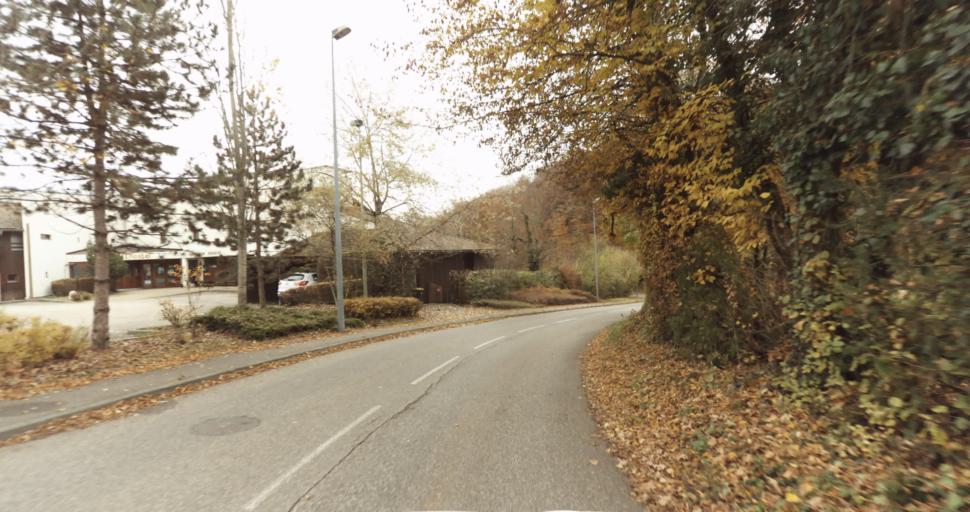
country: FR
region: Rhone-Alpes
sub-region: Departement de la Haute-Savoie
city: Annecy
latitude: 45.8914
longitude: 6.1329
